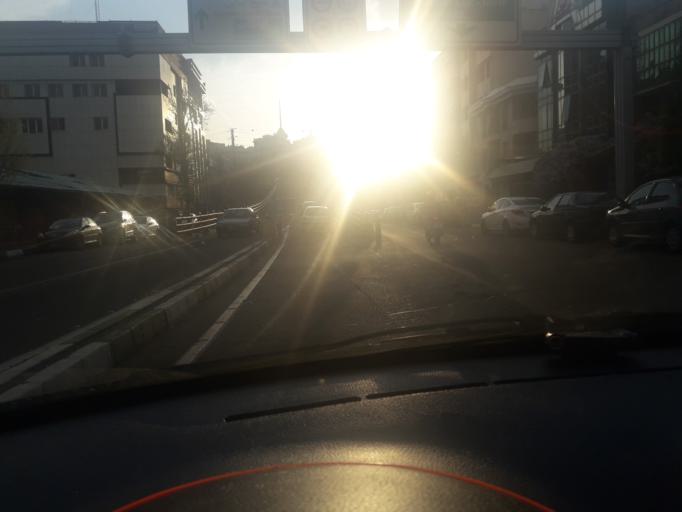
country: IR
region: Tehran
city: Tehran
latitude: 35.7466
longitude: 51.4033
